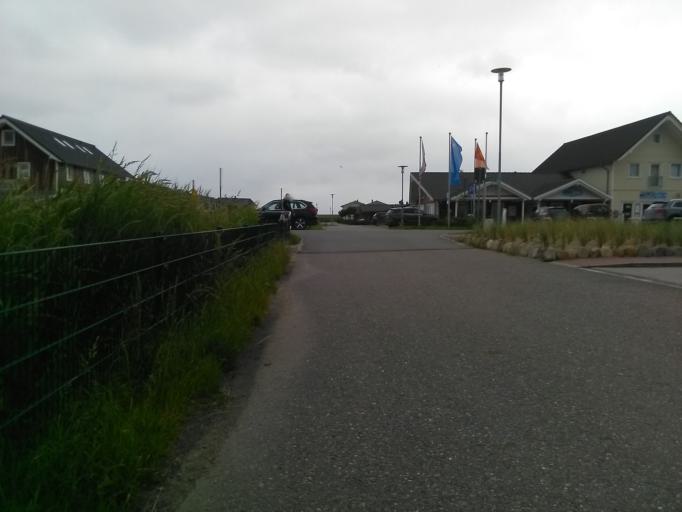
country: DE
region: Schleswig-Holstein
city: Dagebull
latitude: 54.7301
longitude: 8.6979
